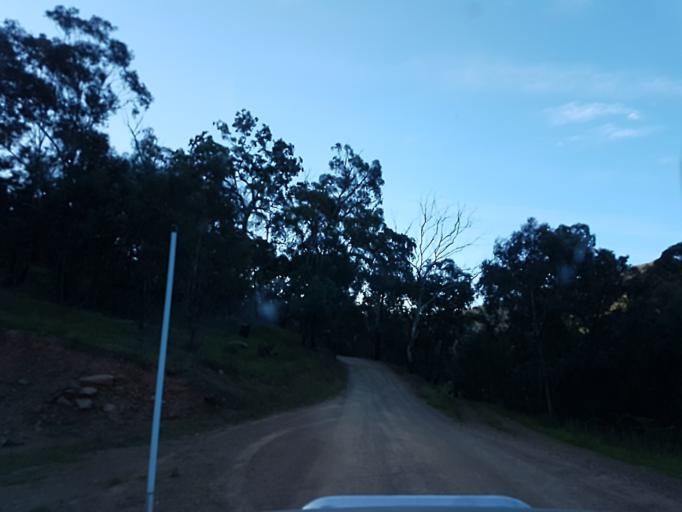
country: AU
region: Victoria
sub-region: Wellington
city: Heyfield
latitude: -37.4076
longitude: 147.0859
